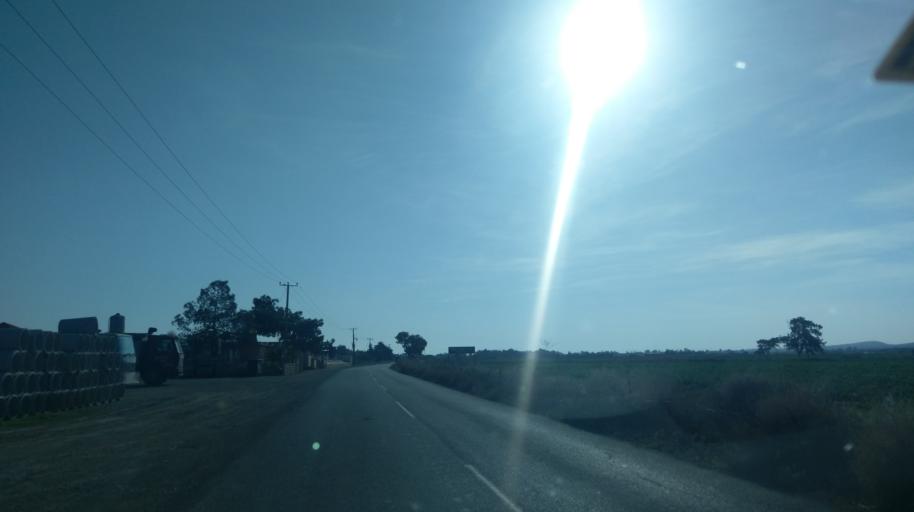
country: CY
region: Larnaka
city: Pergamos
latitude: 35.0611
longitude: 33.7130
